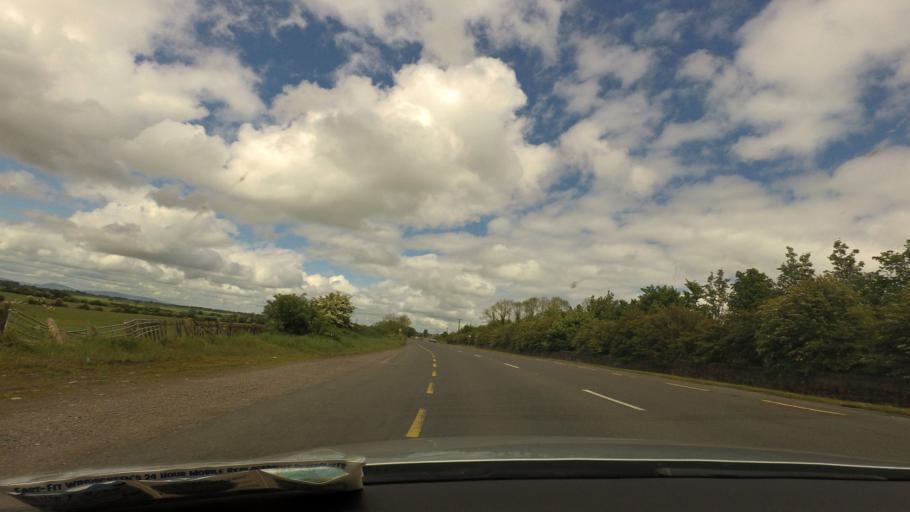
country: IE
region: Munster
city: Cashel
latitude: 52.5363
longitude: -7.8744
